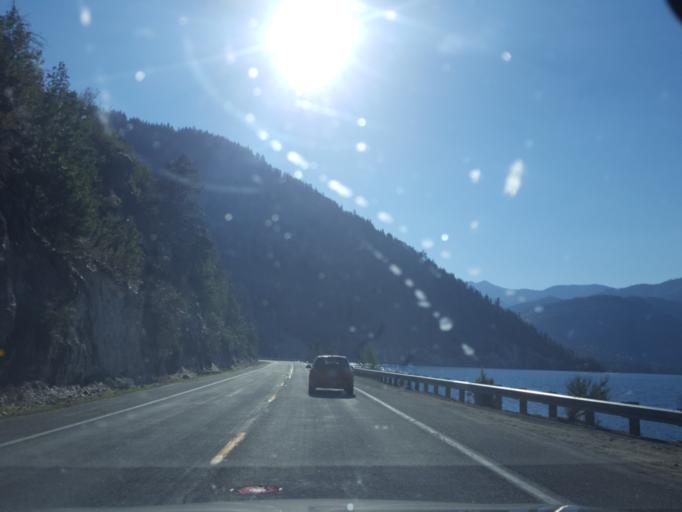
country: US
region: Washington
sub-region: Chelan County
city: Manson
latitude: 47.8604
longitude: -120.1562
